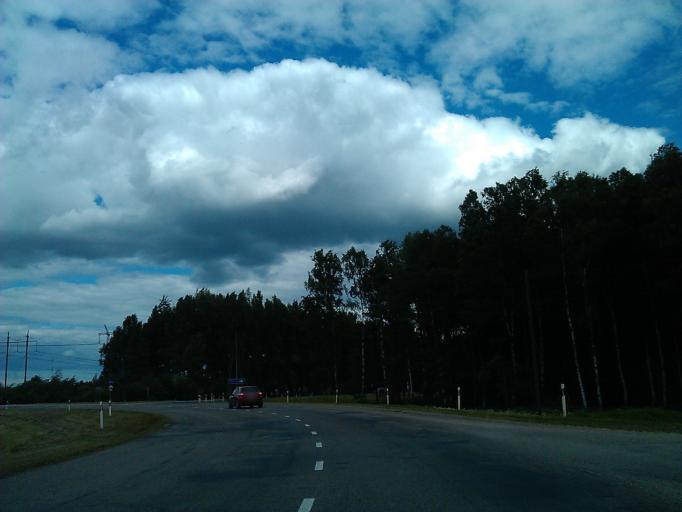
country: LV
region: Jelgava
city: Jelgava
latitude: 56.6290
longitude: 23.7543
